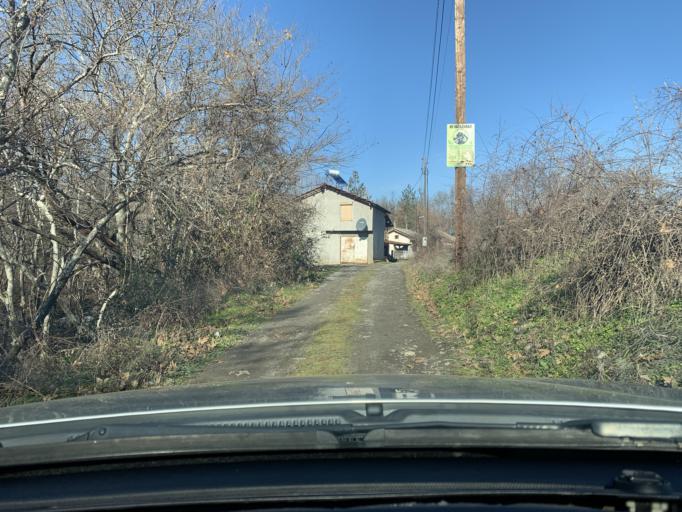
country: MK
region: Demir Kapija
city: Demir Kapija
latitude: 41.3875
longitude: 22.2221
